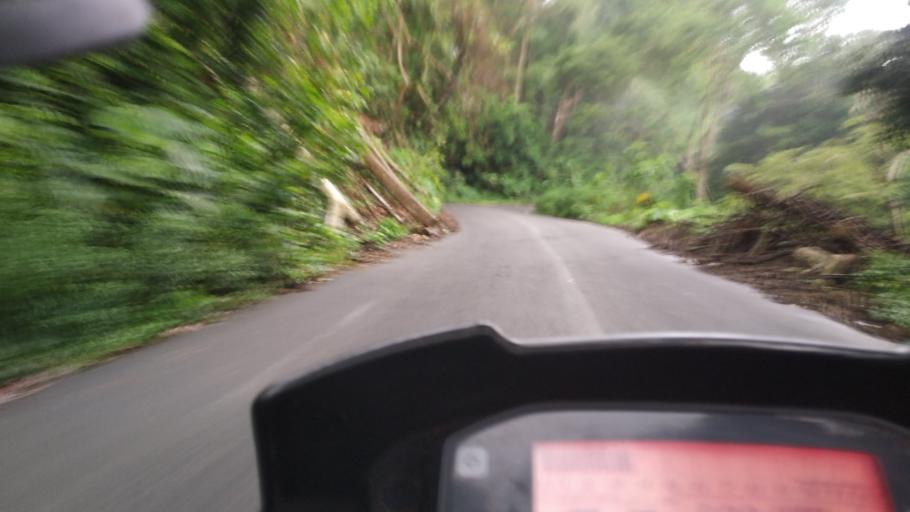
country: IN
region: Kerala
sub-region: Idukki
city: Kuttampuzha
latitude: 10.0656
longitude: 76.7842
